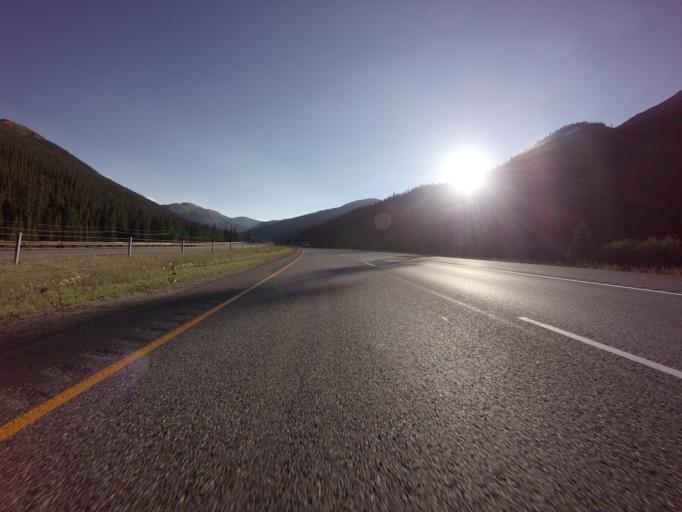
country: US
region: Colorado
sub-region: Summit County
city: Keystone
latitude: 39.7011
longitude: -105.8645
